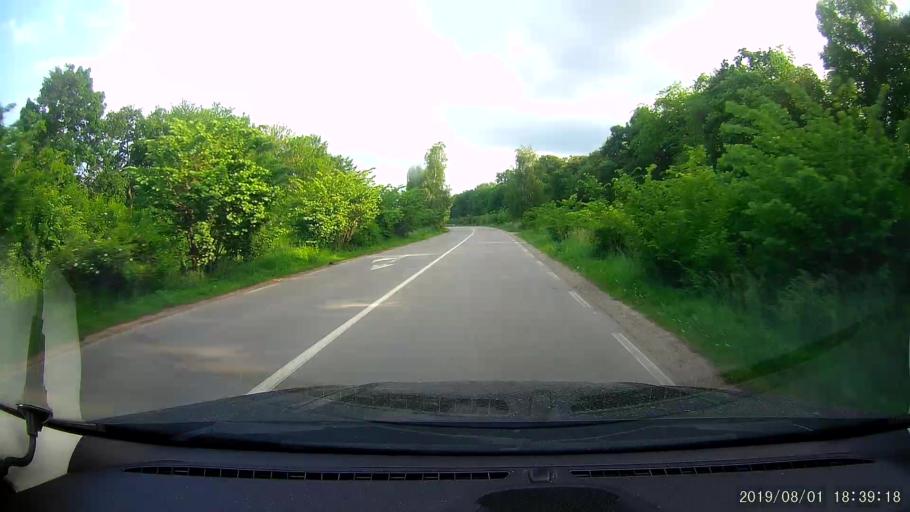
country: BG
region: Shumen
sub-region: Obshtina Khitrino
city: Gara Khitrino
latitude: 43.3885
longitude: 26.9169
